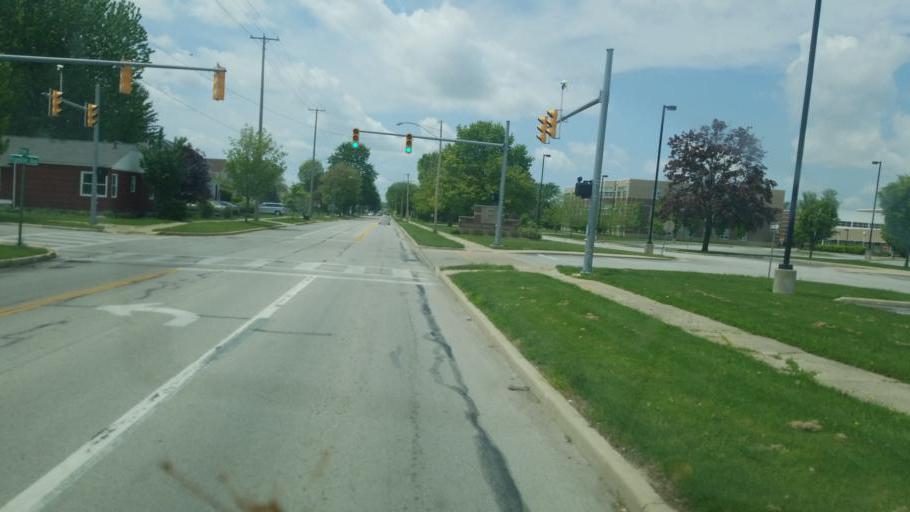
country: US
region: Ohio
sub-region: Sandusky County
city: Fremont
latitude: 41.3614
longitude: -83.1241
